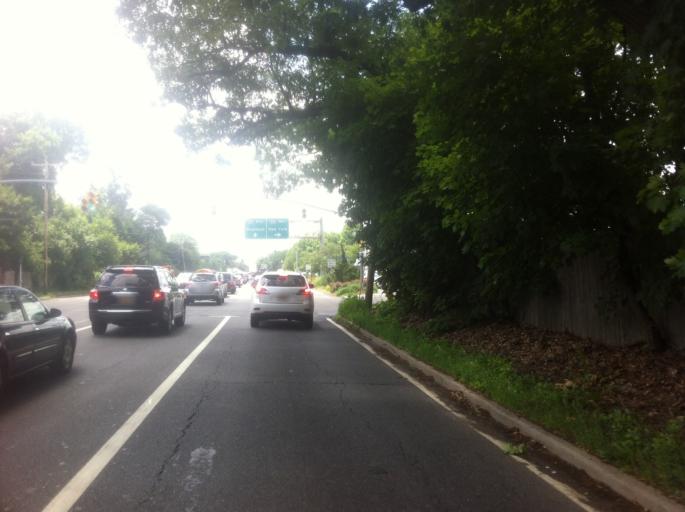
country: US
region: New York
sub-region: Nassau County
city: East Hills
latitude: 40.7862
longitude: -73.6224
